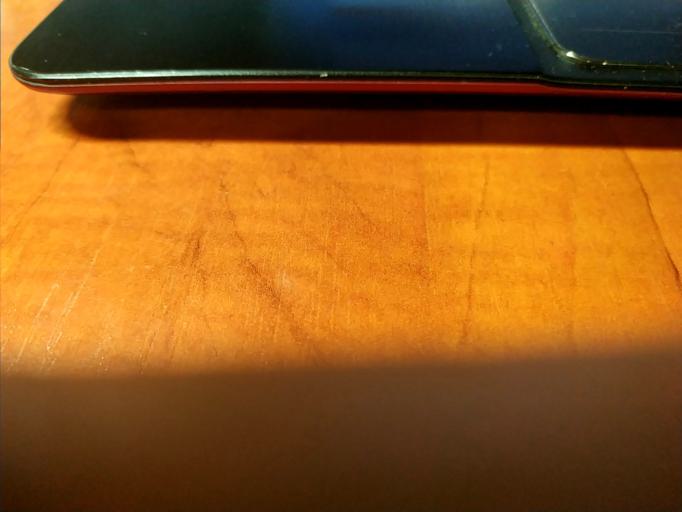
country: RU
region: Smolensk
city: Safonovo
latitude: 55.1844
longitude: 33.0133
